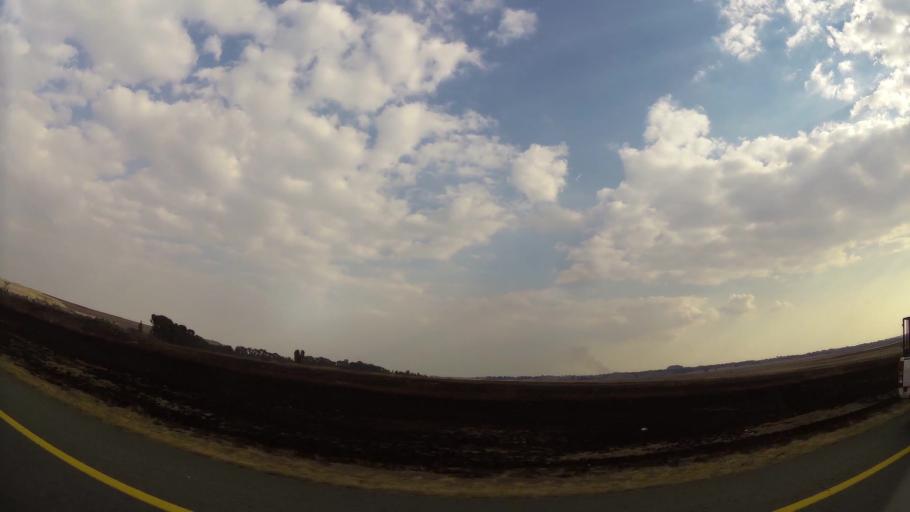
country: ZA
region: Gauteng
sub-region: Ekurhuleni Metropolitan Municipality
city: Springs
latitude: -26.2801
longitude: 28.5233
